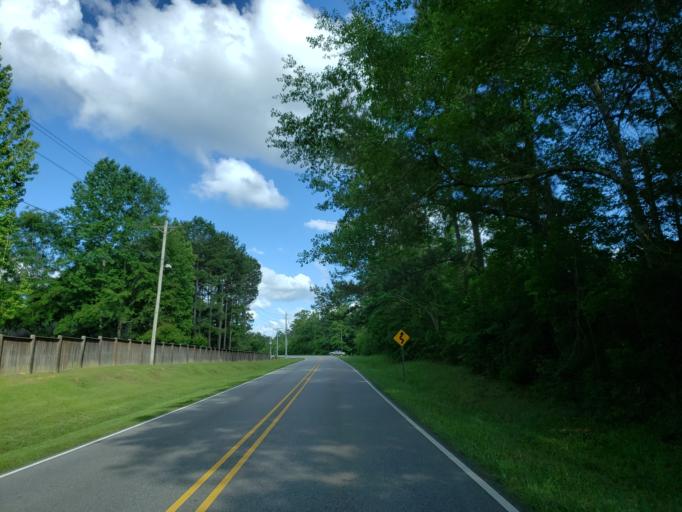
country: US
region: Mississippi
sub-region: Lamar County
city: West Hattiesburg
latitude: 31.2893
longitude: -89.4478
